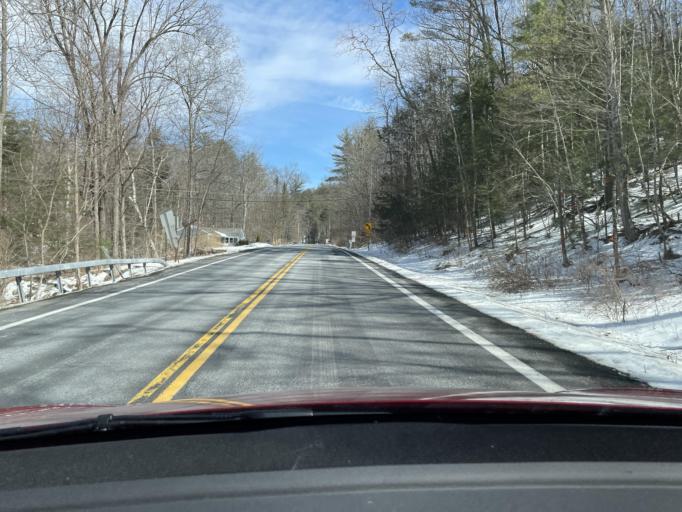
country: US
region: New York
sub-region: Ulster County
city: Shokan
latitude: 42.0497
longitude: -74.2660
